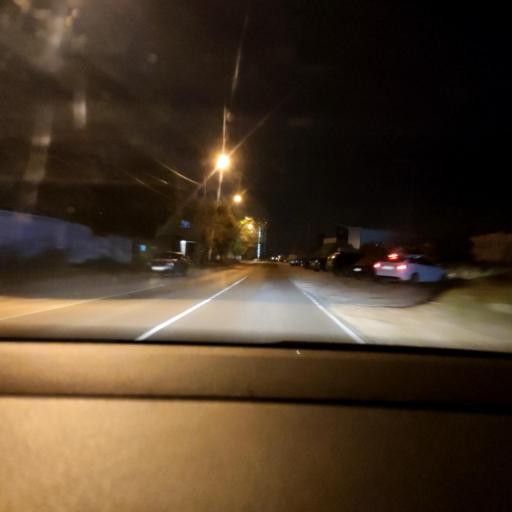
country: RU
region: Moskovskaya
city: Bolshevo
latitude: 55.9387
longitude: 37.8298
